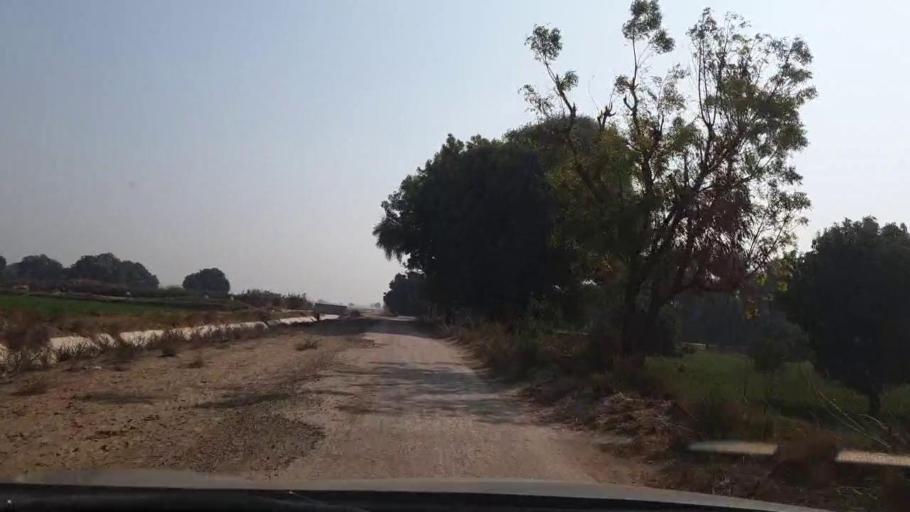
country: PK
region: Sindh
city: Tando Allahyar
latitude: 25.5195
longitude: 68.7850
